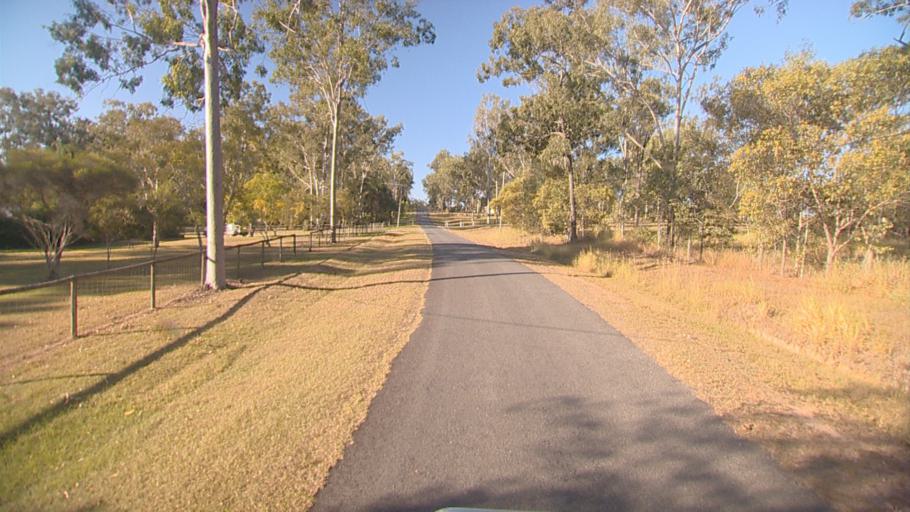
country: AU
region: Queensland
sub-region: Logan
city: North Maclean
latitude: -27.8130
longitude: 153.0457
